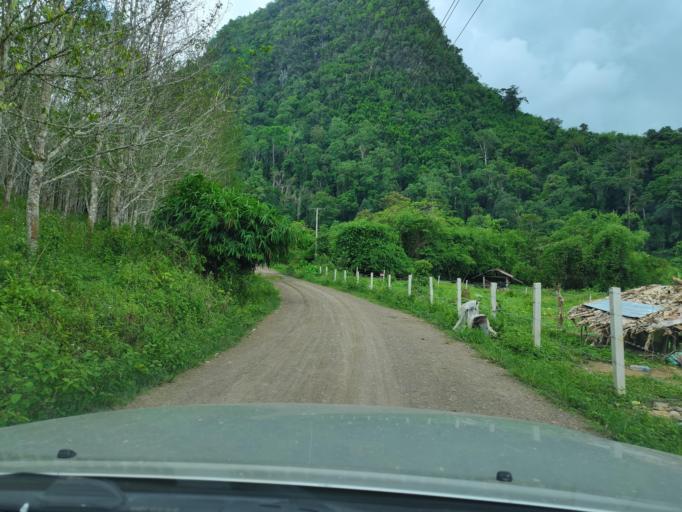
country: LA
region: Loungnamtha
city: Muang Long
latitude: 20.7814
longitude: 101.0167
